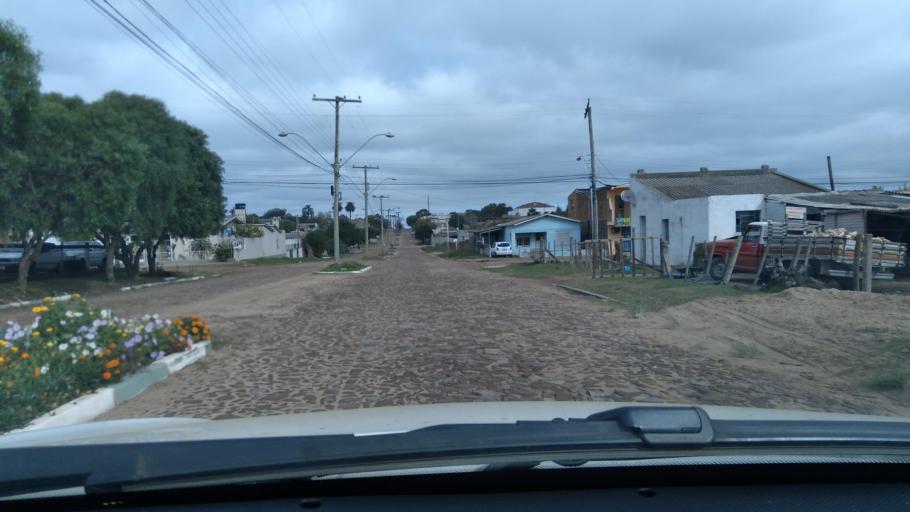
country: BR
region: Rio Grande do Sul
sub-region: Dom Pedrito
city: Dom Pedrito
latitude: -30.9829
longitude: -54.6627
